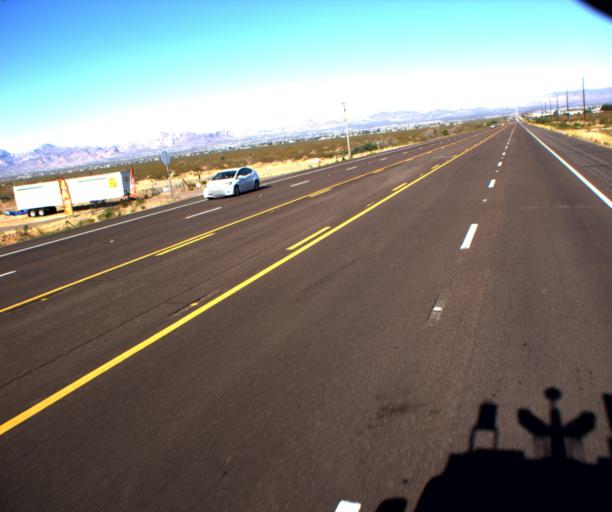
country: US
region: Arizona
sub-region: Mohave County
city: Golden Valley
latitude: 35.2206
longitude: -114.1863
